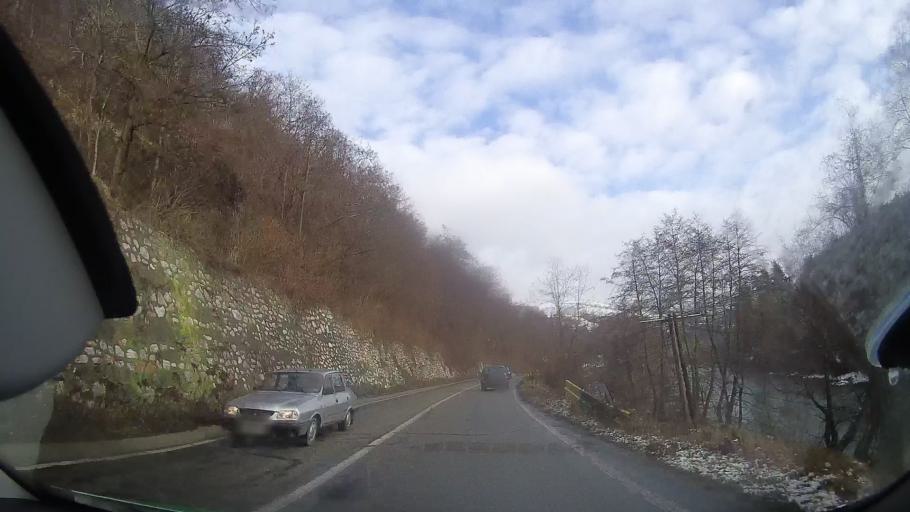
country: RO
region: Alba
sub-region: Oras Baia de Aries
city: Baia de Aries
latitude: 46.3887
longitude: 23.2806
